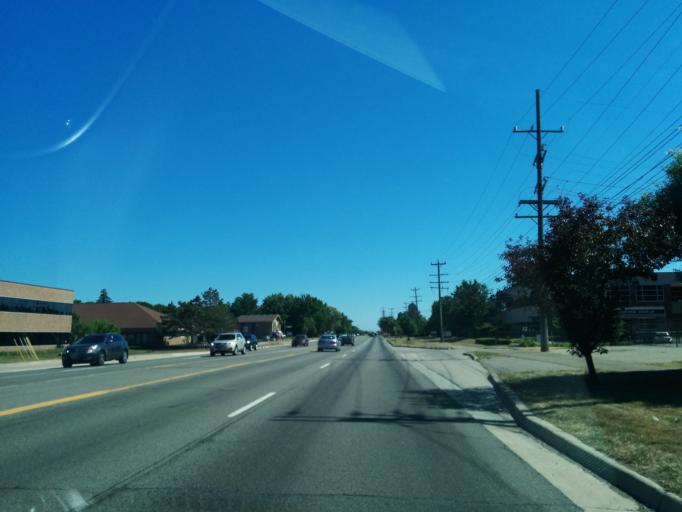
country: US
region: Michigan
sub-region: Oakland County
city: Farmington Hills
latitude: 42.5211
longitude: -83.3598
